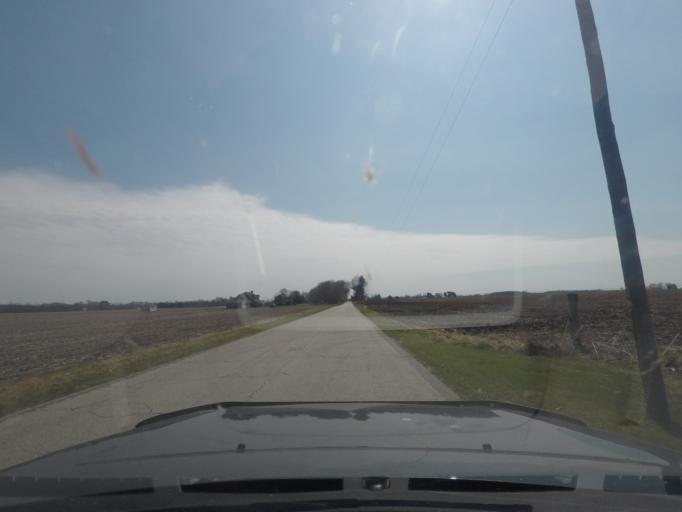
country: US
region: Indiana
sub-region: LaPorte County
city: LaPorte
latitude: 41.5768
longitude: -86.7982
